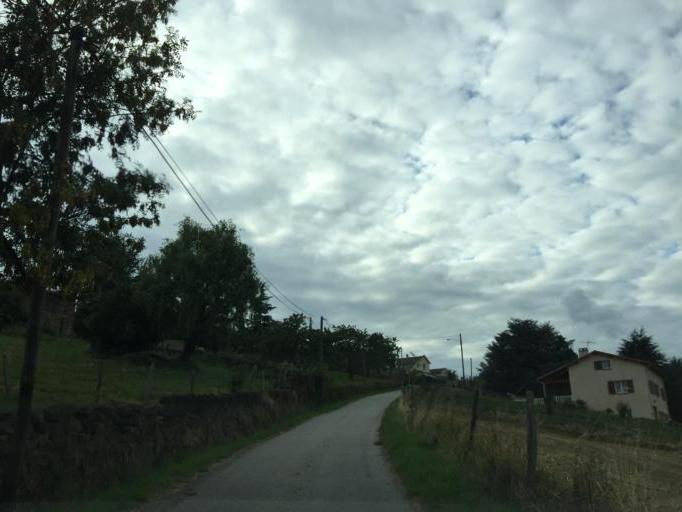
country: FR
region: Rhone-Alpes
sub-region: Departement de la Loire
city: Saint-Chamond
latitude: 45.4850
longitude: 4.4913
